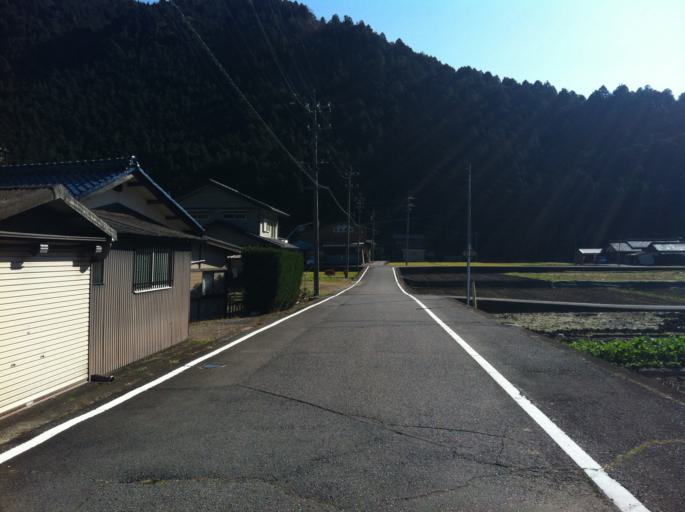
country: JP
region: Gifu
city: Minokamo
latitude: 35.6193
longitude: 137.1670
